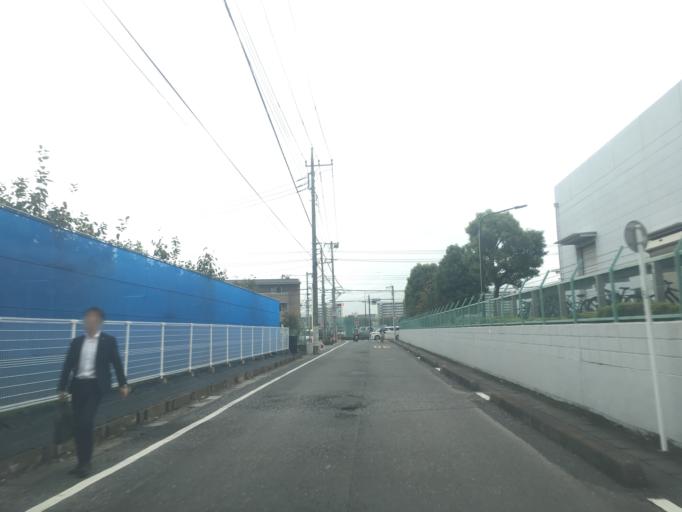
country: JP
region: Tokyo
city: Higashimurayama-shi
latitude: 35.7574
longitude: 139.4602
